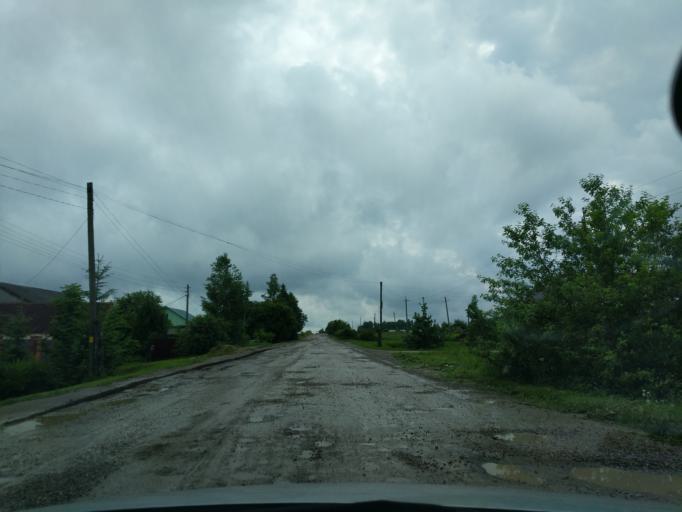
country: RU
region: Kaluga
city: Myatlevo
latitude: 54.7931
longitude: 35.7373
